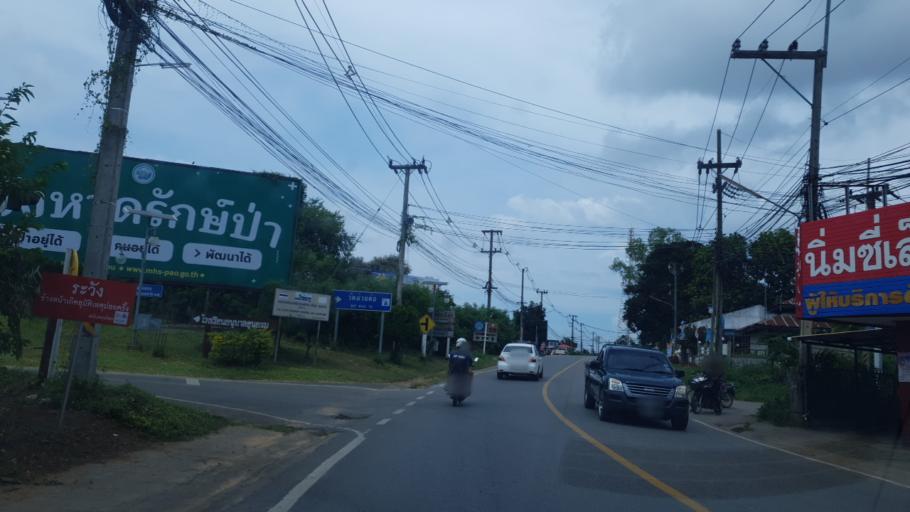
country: TH
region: Mae Hong Son
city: Khun Yuam
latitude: 18.8277
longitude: 97.9328
